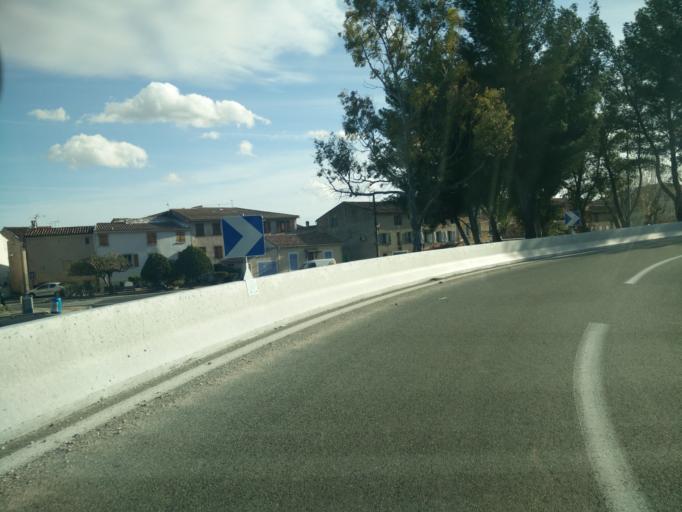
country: FR
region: Provence-Alpes-Cote d'Azur
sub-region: Departement du Var
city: Sollies-Pont
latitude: 43.1963
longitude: 6.0426
